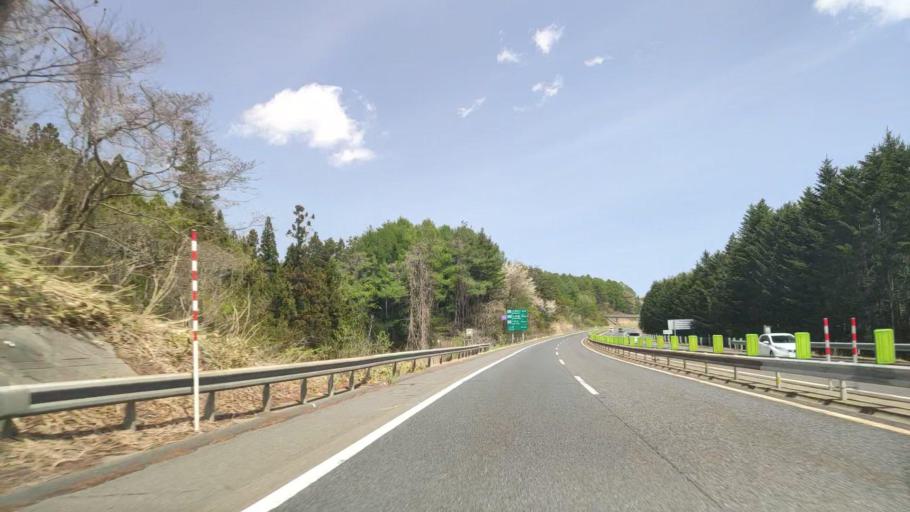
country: JP
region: Aomori
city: Hachinohe
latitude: 40.4253
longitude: 141.4393
